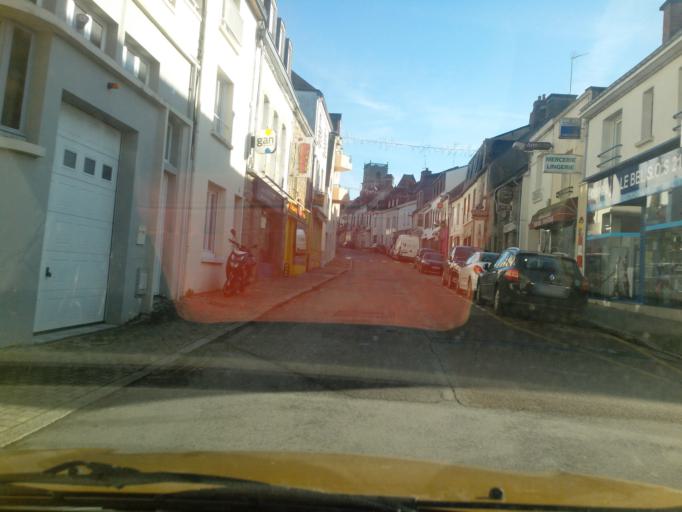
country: FR
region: Brittany
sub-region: Departement du Morbihan
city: Ploermel
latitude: 47.9328
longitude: -2.4020
